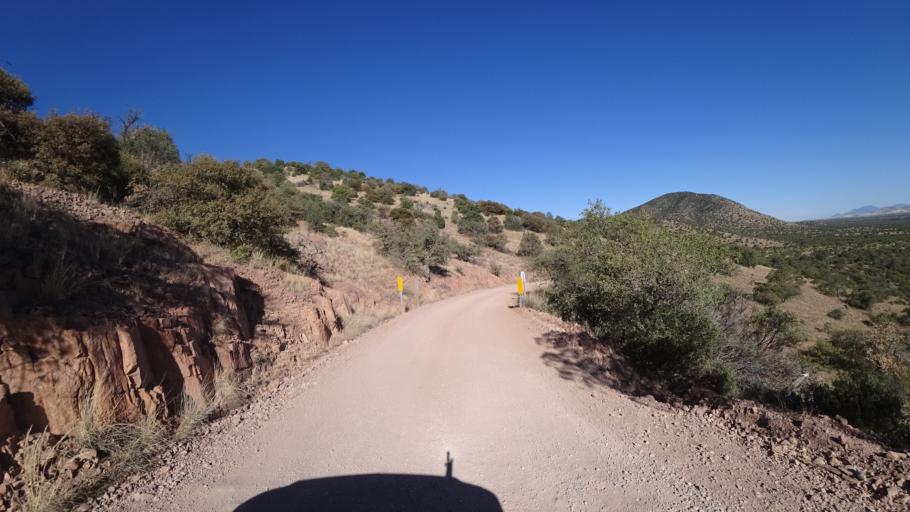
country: US
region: Arizona
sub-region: Cochise County
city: Huachuca City
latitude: 31.4991
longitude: -110.5579
